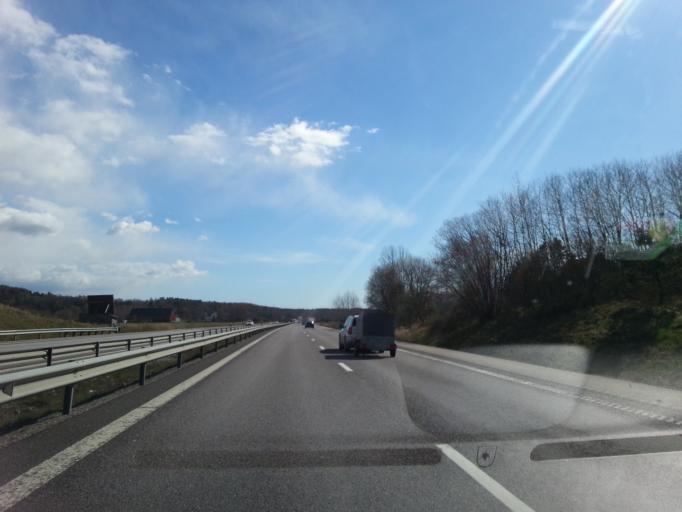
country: SE
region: Vaestra Goetaland
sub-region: Stenungsunds Kommun
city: Stora Hoga
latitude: 57.9854
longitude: 11.8419
